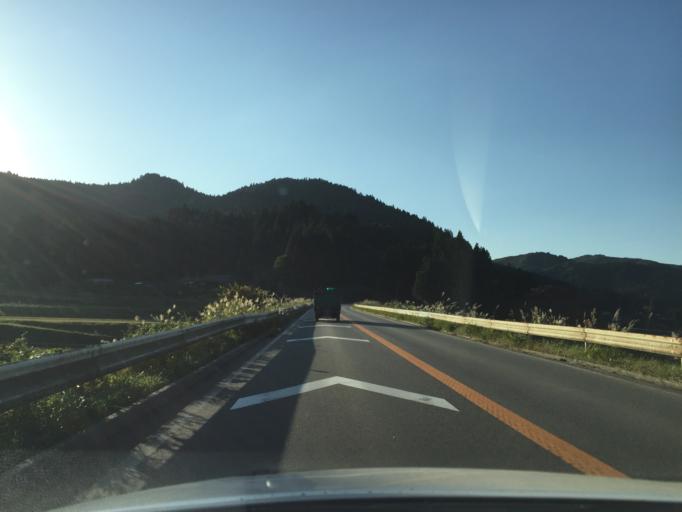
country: JP
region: Fukushima
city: Ishikawa
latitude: 37.1472
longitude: 140.6692
